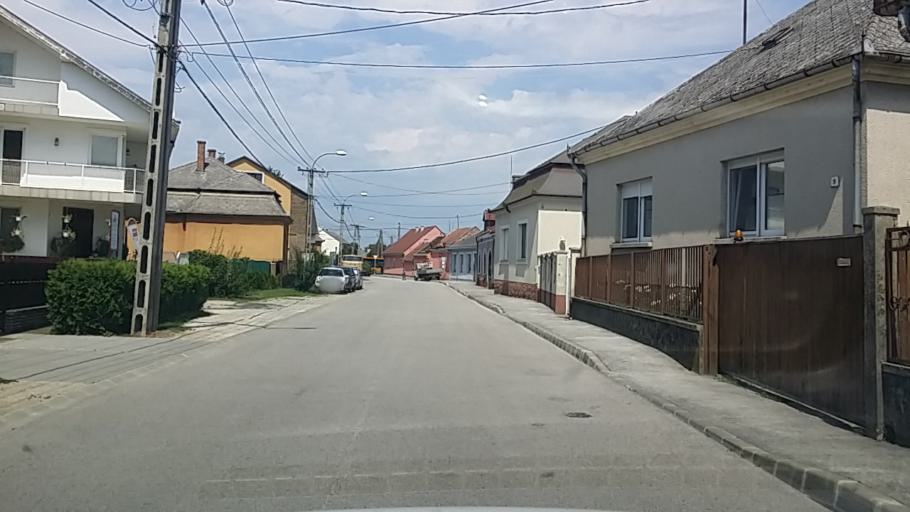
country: HU
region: Zala
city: Nagykanizsa
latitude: 46.4520
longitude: 16.9647
